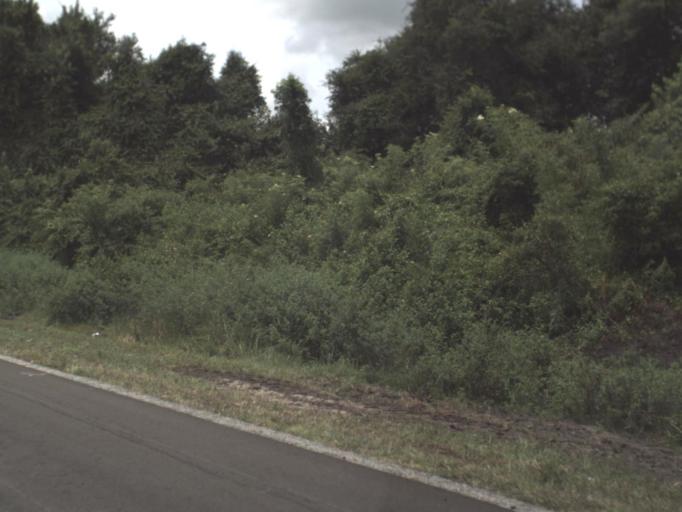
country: US
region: Florida
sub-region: Pasco County
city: San Antonio
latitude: 28.4038
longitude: -82.3075
